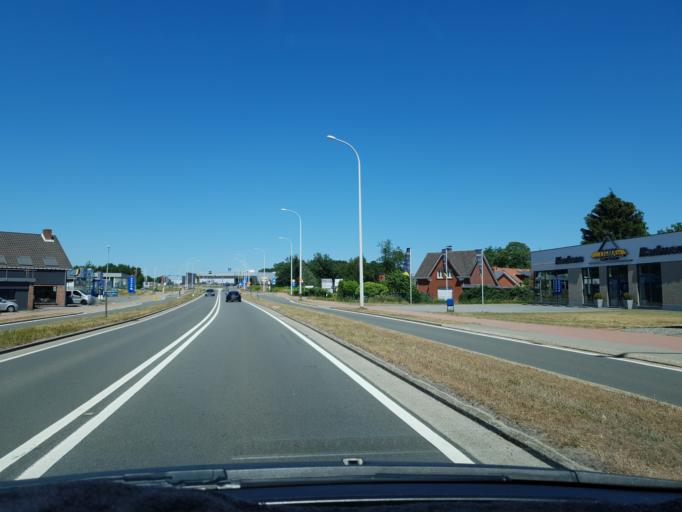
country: BE
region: Flanders
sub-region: Provincie Antwerpen
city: Herentals
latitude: 51.1660
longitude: 4.8468
